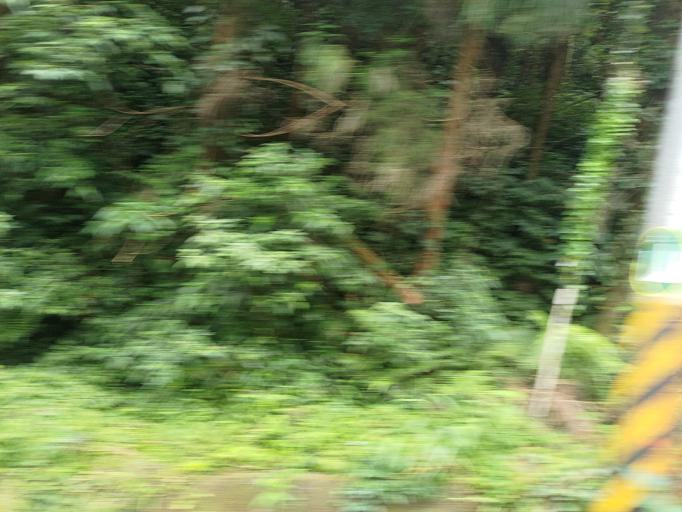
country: TW
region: Taiwan
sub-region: Hsinchu
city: Hsinchu
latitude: 24.6295
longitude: 121.0773
